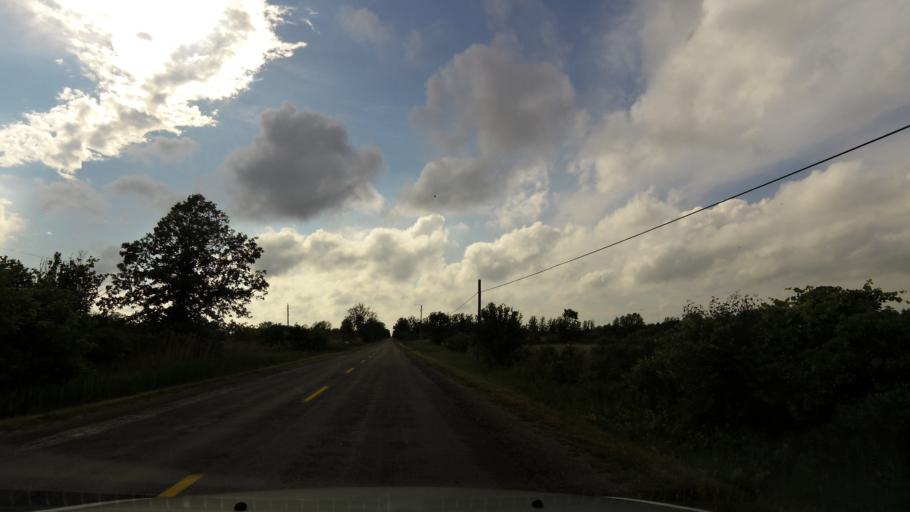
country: CA
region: Ontario
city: Ancaster
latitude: 43.0093
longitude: -80.0687
